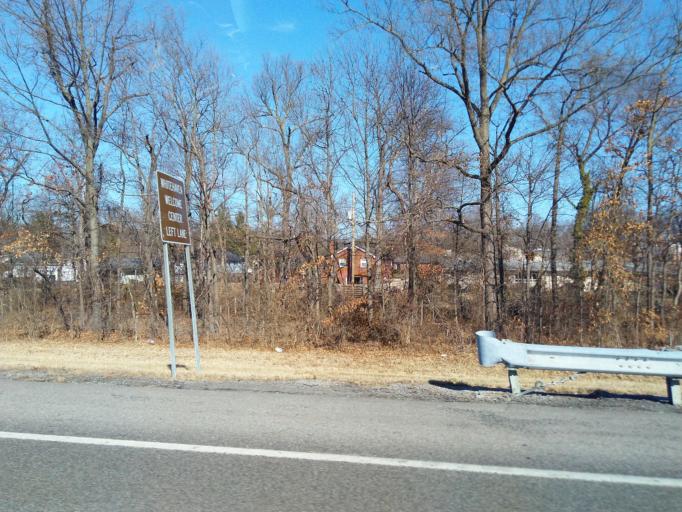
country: US
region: Kentucky
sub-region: McCracken County
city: Hendron
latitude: 37.0539
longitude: -88.6515
